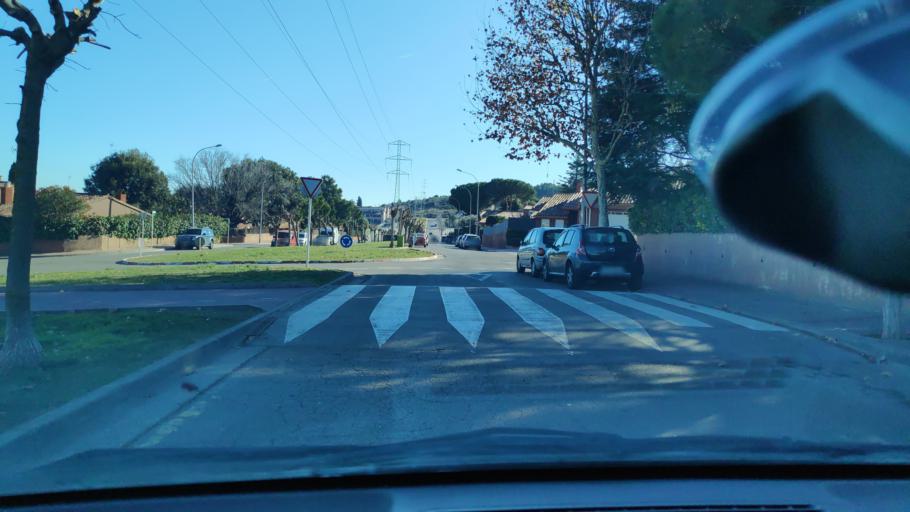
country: ES
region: Catalonia
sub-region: Provincia de Barcelona
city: Sant Quirze del Valles
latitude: 41.5294
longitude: 2.0757
